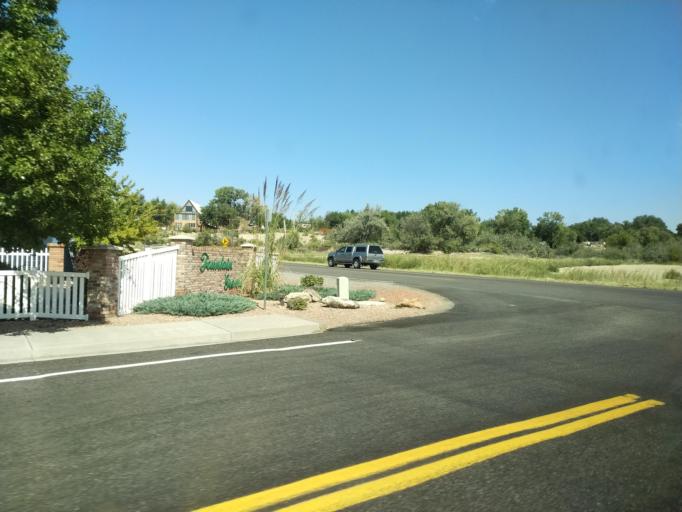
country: US
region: Colorado
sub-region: Mesa County
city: Redlands
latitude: 39.1095
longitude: -108.5899
